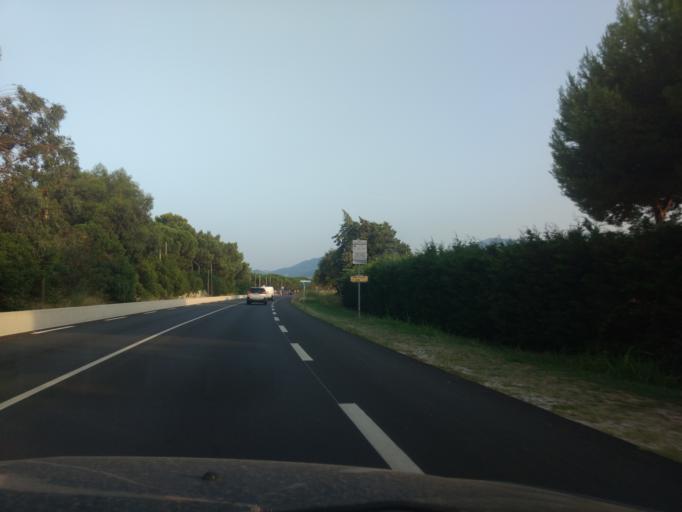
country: FR
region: Languedoc-Roussillon
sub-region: Departement des Pyrenees-Orientales
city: Argelers
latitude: 42.5713
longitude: 3.0403
